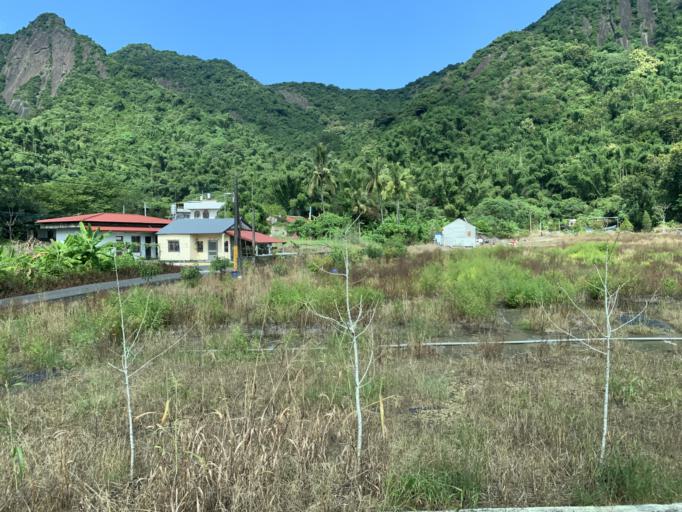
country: TW
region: Taiwan
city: Yujing
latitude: 22.9025
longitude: 120.5180
